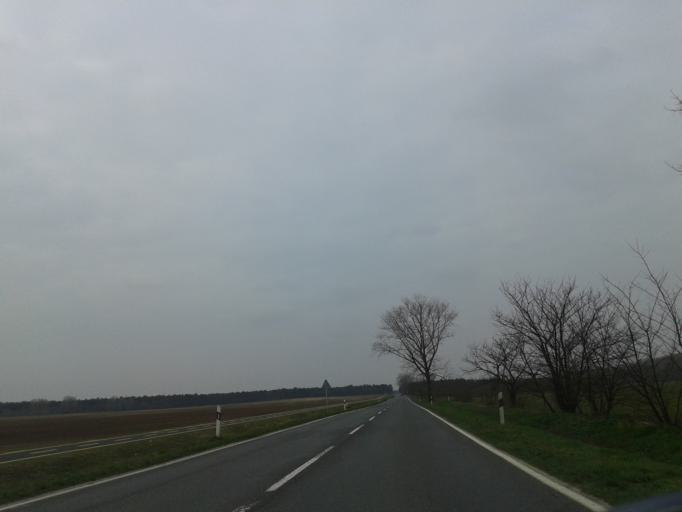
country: HU
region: Gyor-Moson-Sopron
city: Toltestava
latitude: 47.7281
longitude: 17.7349
